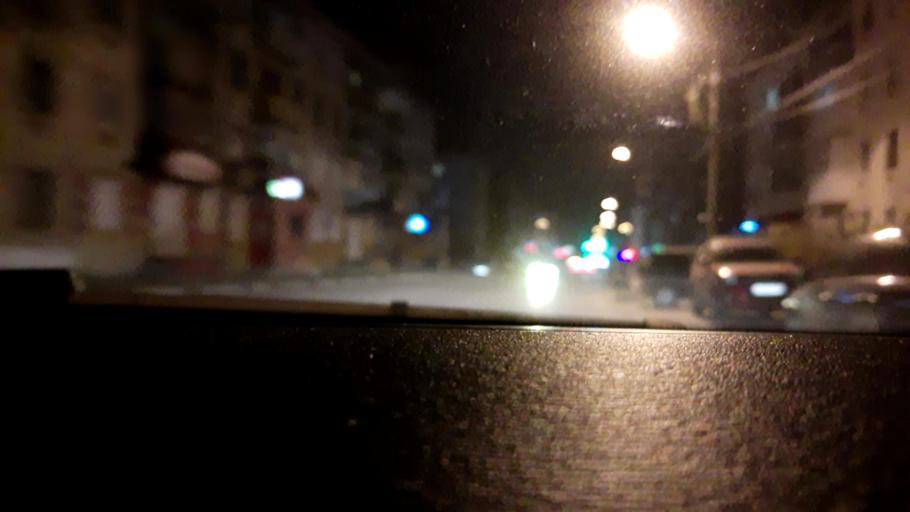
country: RU
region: Nizjnij Novgorod
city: Kstovo
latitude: 56.1478
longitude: 44.2044
